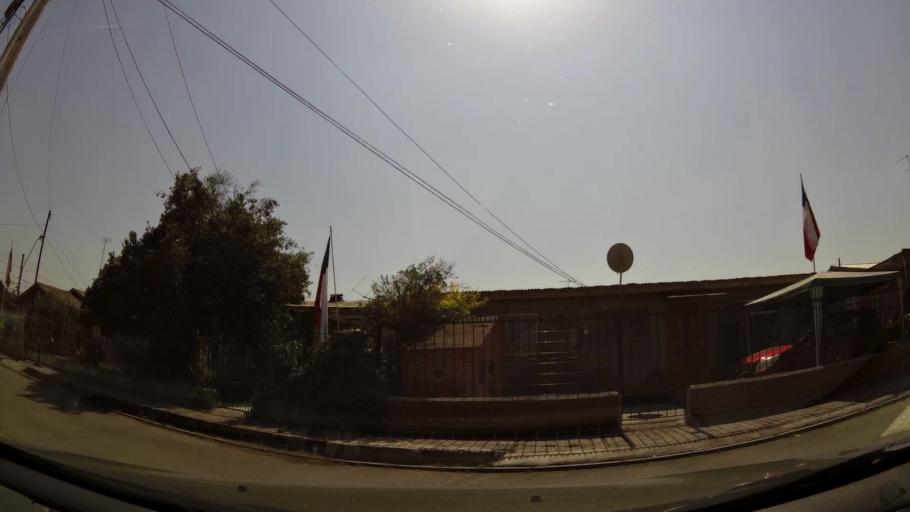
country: CL
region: Santiago Metropolitan
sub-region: Provincia de Maipo
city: San Bernardo
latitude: -33.5832
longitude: -70.7106
